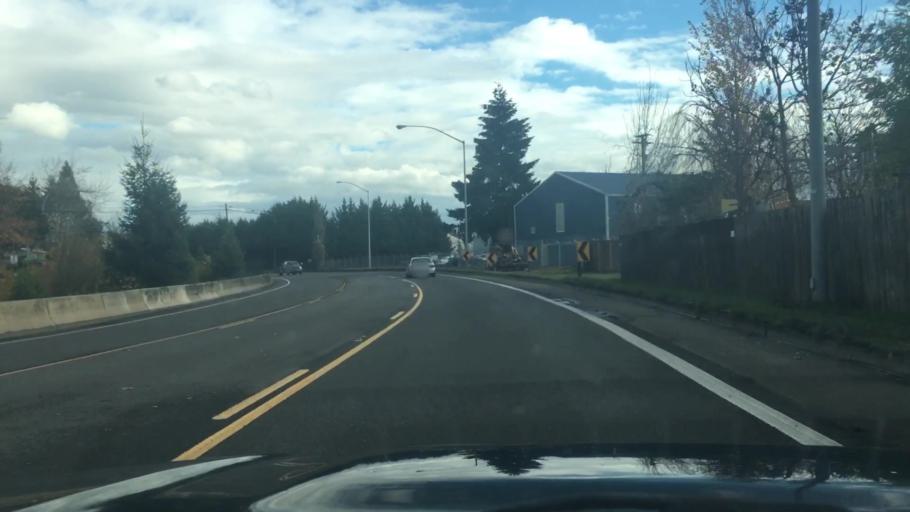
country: US
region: Oregon
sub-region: Lane County
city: Eugene
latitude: 44.0635
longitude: -123.1582
